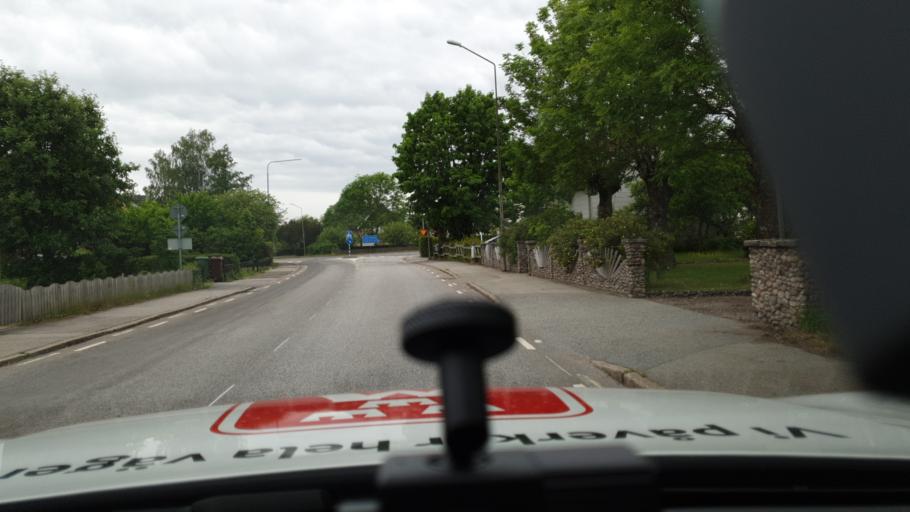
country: SE
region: Vaestra Goetaland
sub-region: Toreboda Kommun
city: Toereboda
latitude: 58.7103
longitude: 14.1371
